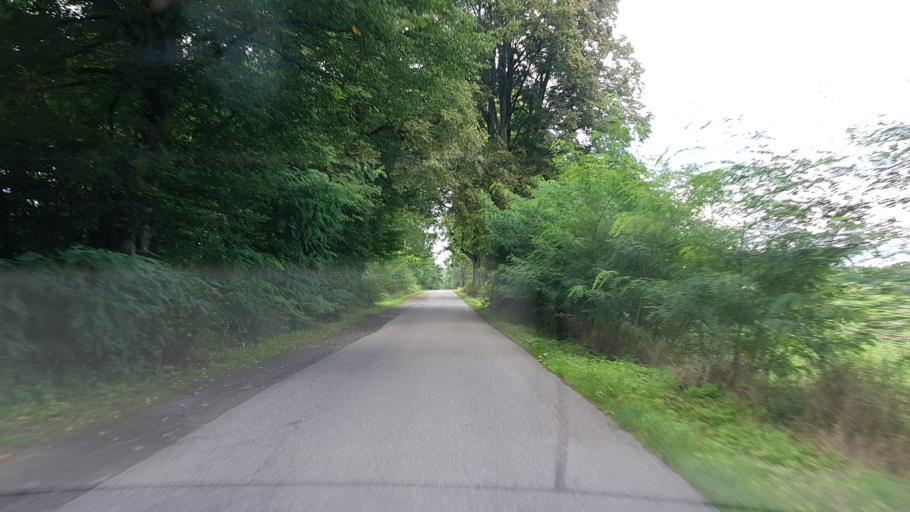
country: PL
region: West Pomeranian Voivodeship
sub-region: Powiat bialogardzki
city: Tychowo
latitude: 54.0259
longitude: 16.3566
